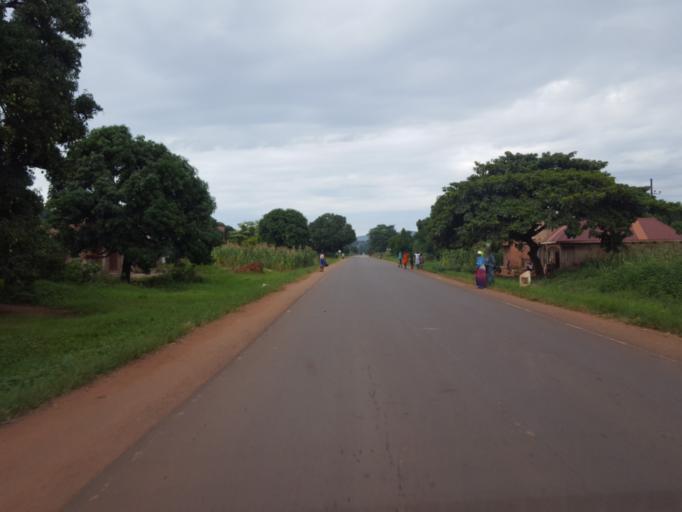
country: UG
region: Central Region
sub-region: Kiboga District
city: Kiboga
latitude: 1.0271
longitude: 31.6814
